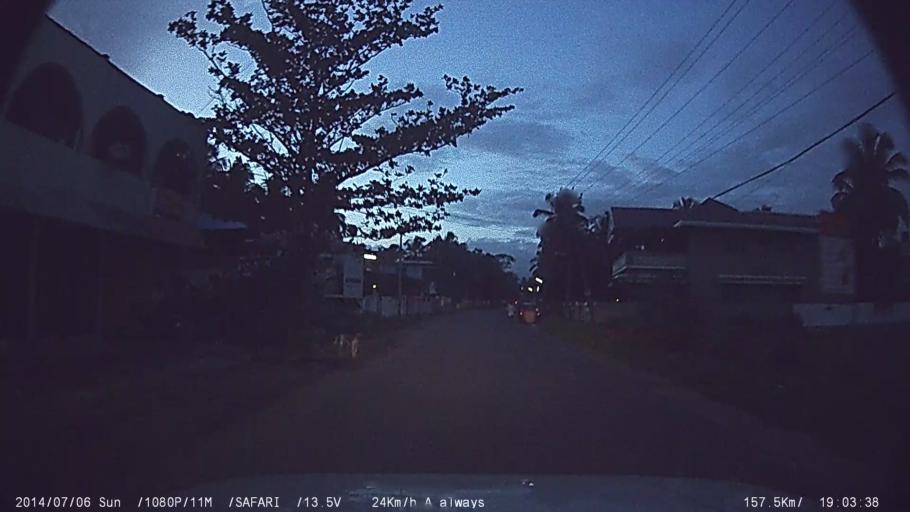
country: IN
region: Kerala
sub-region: Palakkad district
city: Palakkad
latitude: 10.7406
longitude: 76.6468
